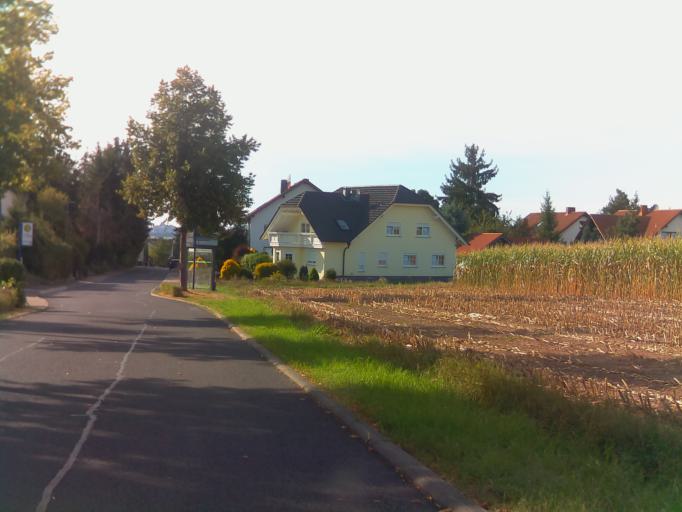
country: DE
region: Hesse
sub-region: Regierungsbezirk Kassel
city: Dipperz
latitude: 50.5416
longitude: 9.8080
